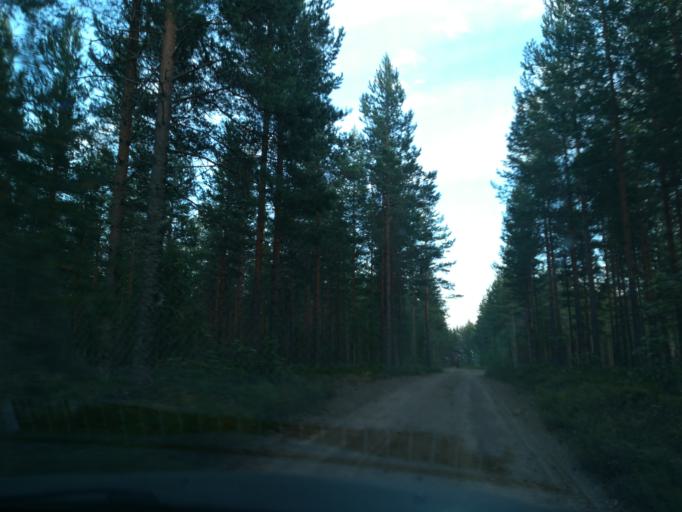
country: FI
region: South Karelia
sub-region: Lappeenranta
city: Joutseno
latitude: 61.3407
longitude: 28.4058
